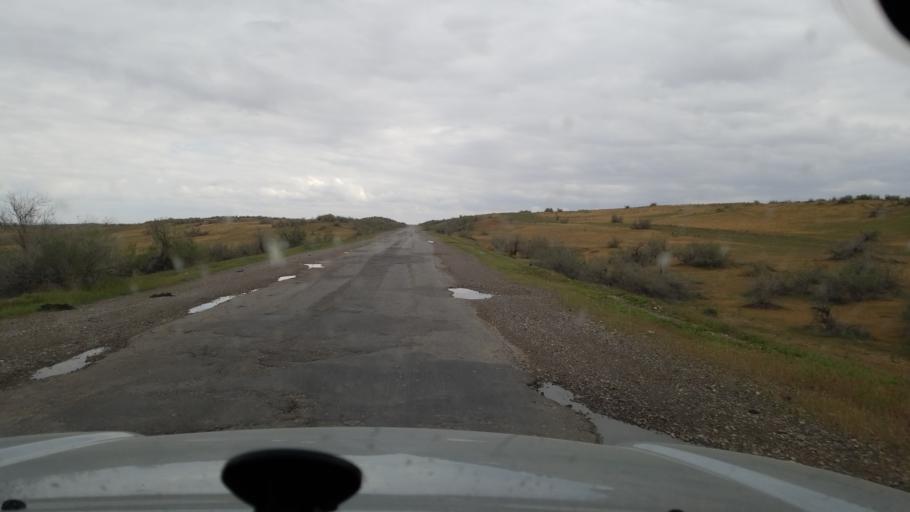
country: TM
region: Mary
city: Serhetabat
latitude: 36.1018
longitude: 62.6100
